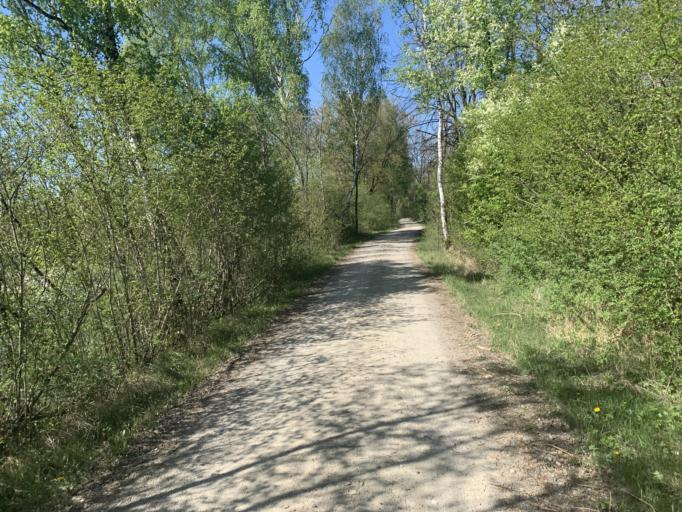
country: DE
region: Bavaria
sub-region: Swabia
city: Gersthofen
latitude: 48.4471
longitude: 10.8880
